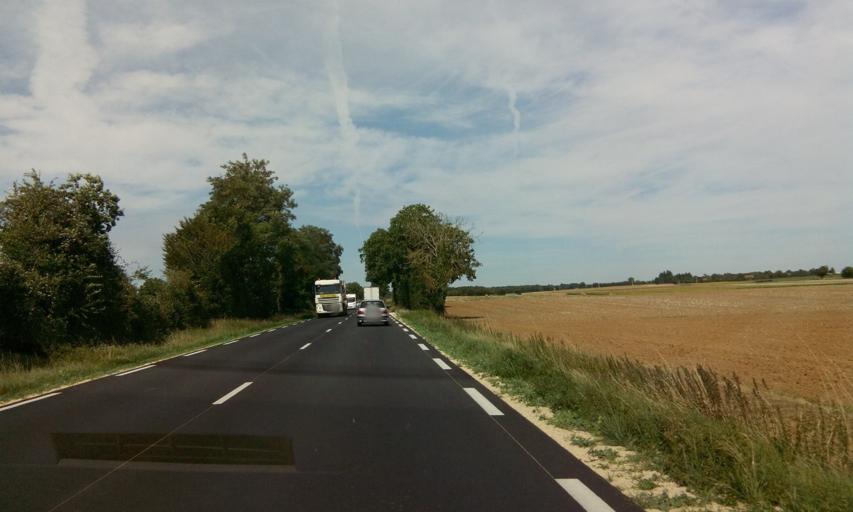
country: FR
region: Poitou-Charentes
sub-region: Departement des Deux-Sevres
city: Sauze-Vaussais
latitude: 46.1435
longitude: 0.0839
